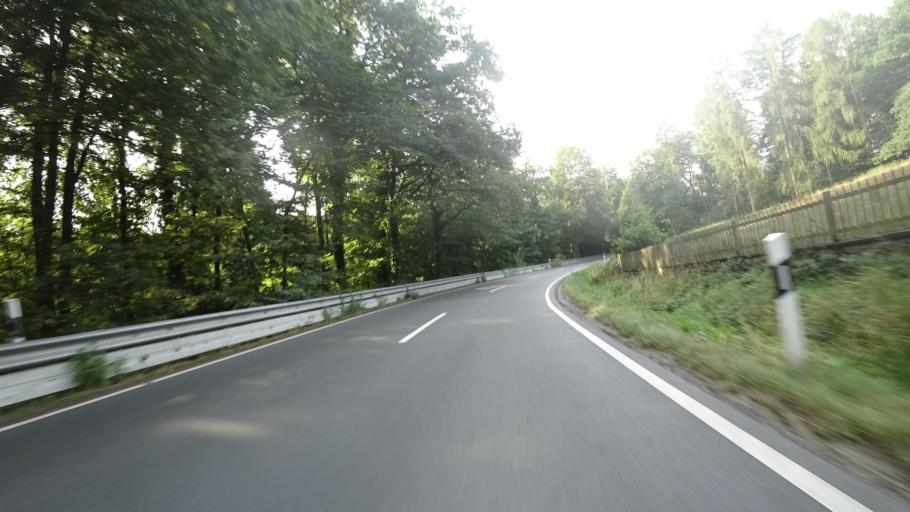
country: DE
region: North Rhine-Westphalia
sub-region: Regierungsbezirk Detmold
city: Steinhagen
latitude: 52.0192
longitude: 8.4518
